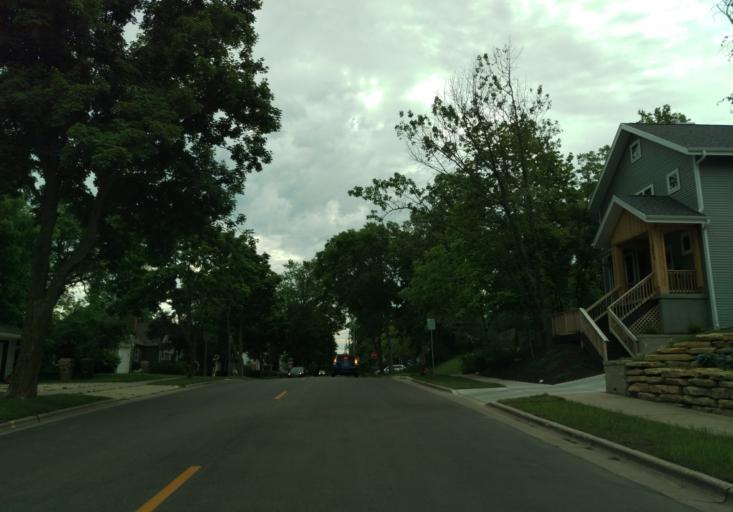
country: US
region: Wisconsin
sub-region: Dane County
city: Shorewood Hills
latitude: 43.0715
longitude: -89.4373
